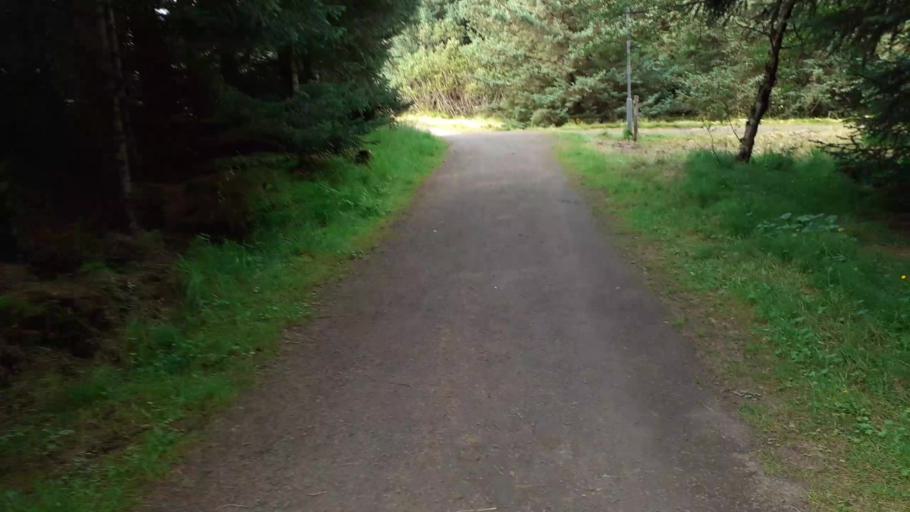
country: IS
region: Northeast
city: Akureyri
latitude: 65.6415
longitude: -18.0959
